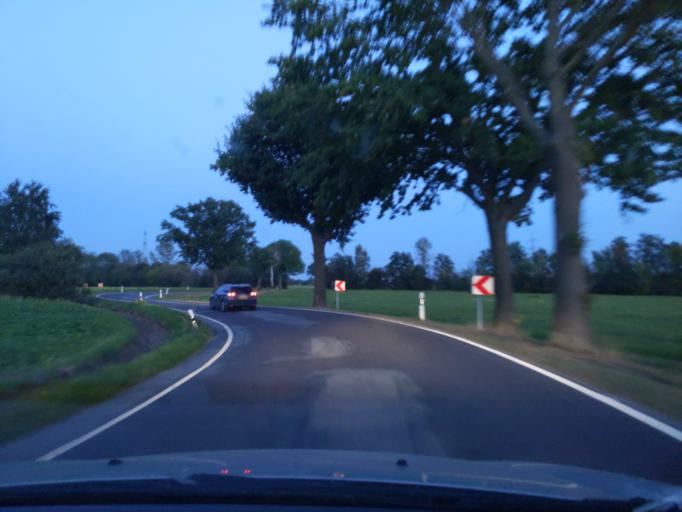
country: DE
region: Saxony
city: Grossdubrau
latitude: 51.3012
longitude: 14.4373
